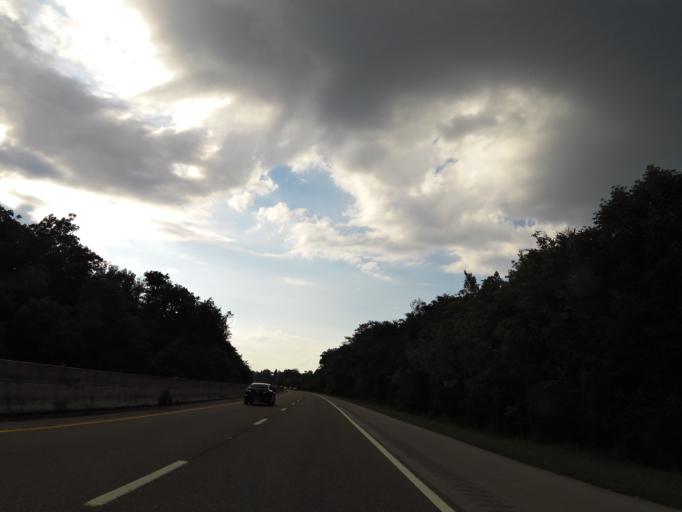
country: US
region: Tennessee
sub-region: Blount County
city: Louisville
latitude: 35.8574
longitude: -84.0247
